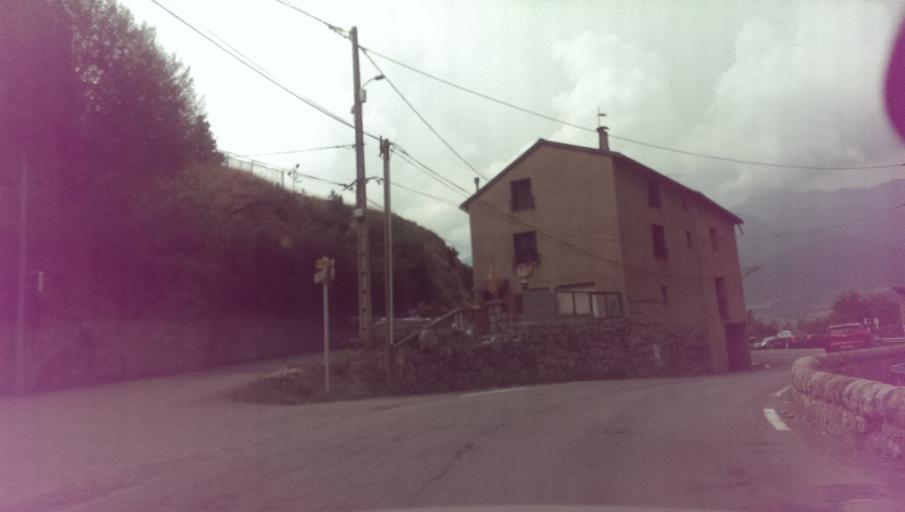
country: ES
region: Catalonia
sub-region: Provincia de Girona
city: Llivia
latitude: 42.5104
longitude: 2.1292
